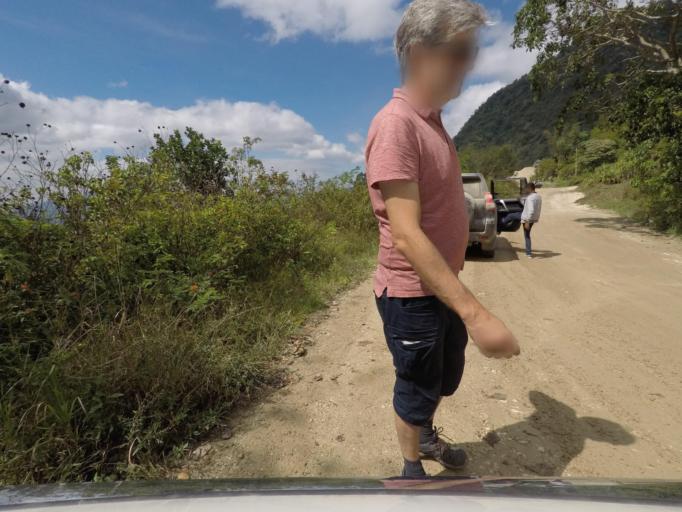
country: TL
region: Baucau
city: Venilale
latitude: -8.7102
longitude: 126.3641
